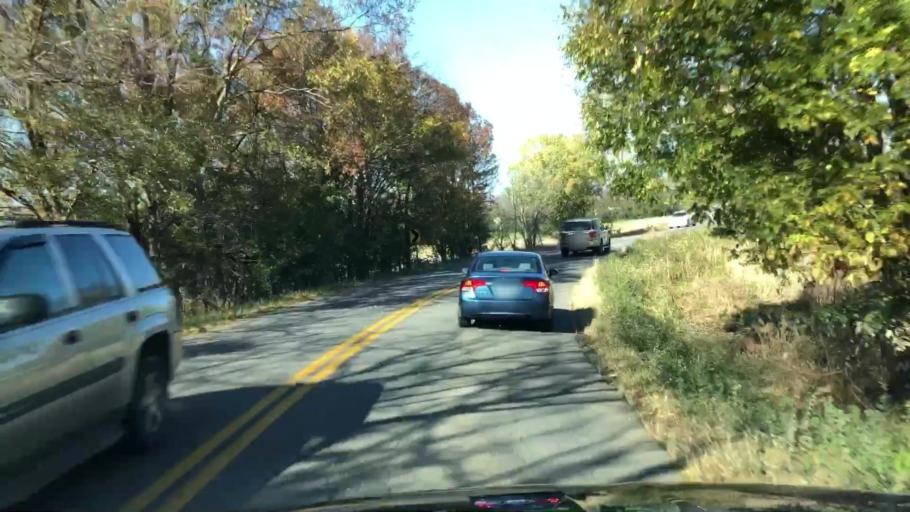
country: US
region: Virginia
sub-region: Fauquier County
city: Bealeton
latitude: 38.5290
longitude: -77.8067
